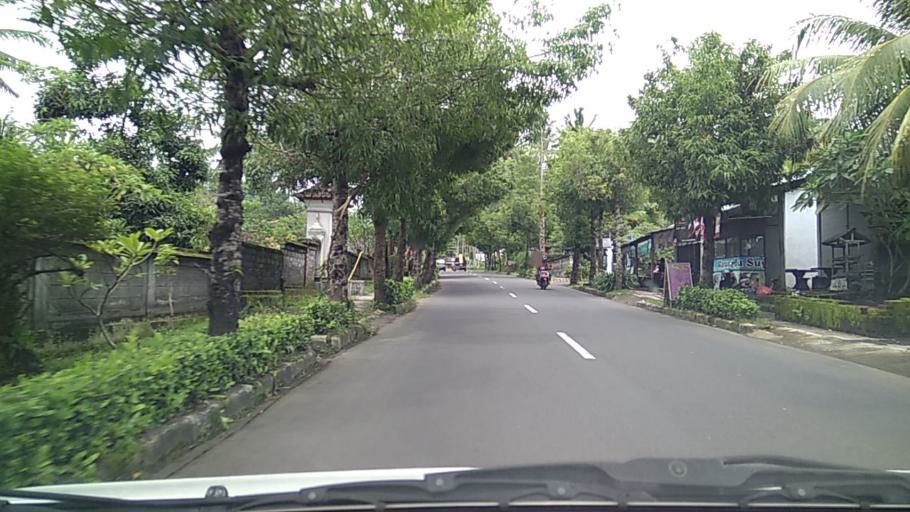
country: ID
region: Bali
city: Banjar Kelodan
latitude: -8.5282
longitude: 115.3481
